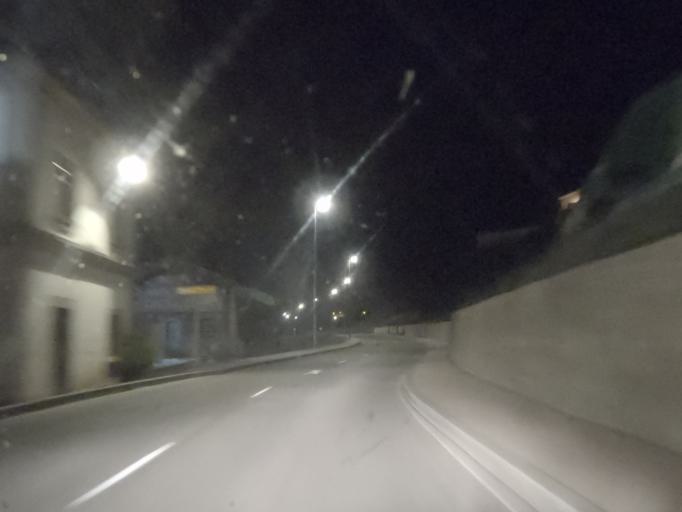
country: ES
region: Castille and Leon
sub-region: Provincia de Zamora
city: Benavente
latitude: 42.0002
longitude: -5.6832
